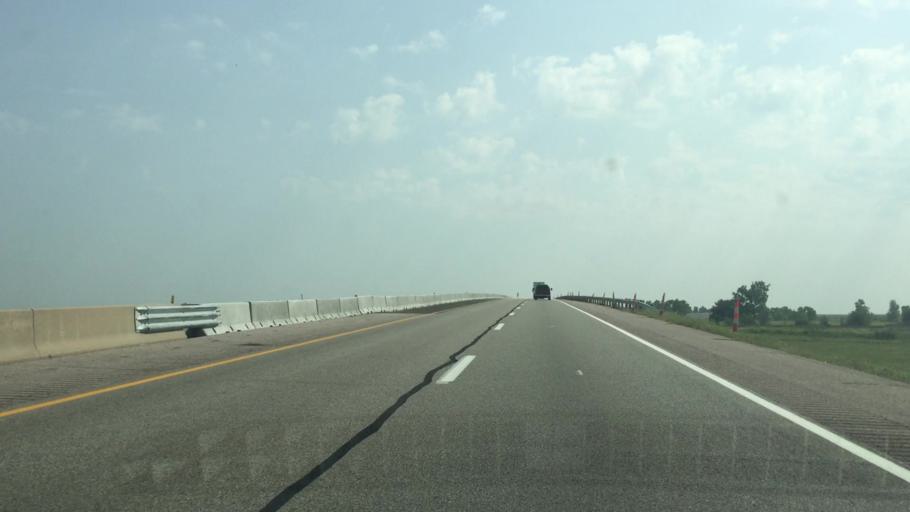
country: US
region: Kansas
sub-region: Chase County
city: Cottonwood Falls
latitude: 38.0609
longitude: -96.6188
